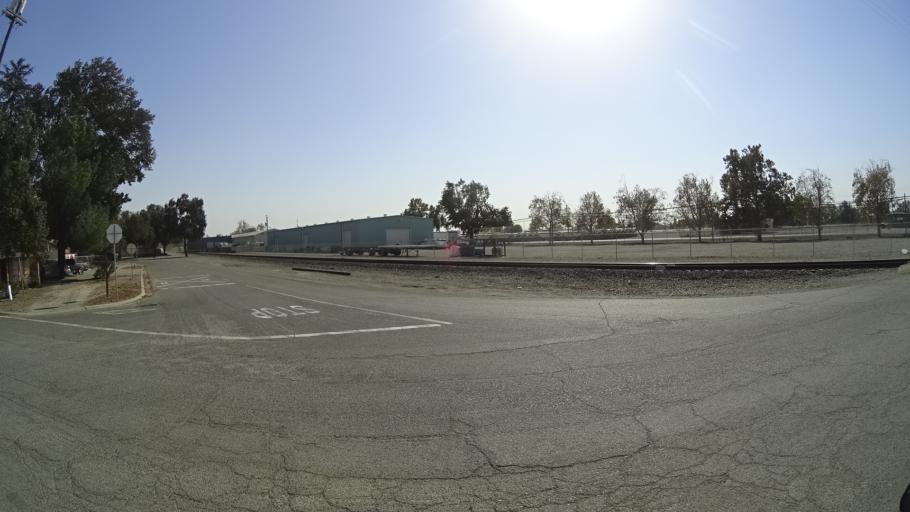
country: US
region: California
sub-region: Yolo County
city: Woodland
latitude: 38.7353
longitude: -121.8144
